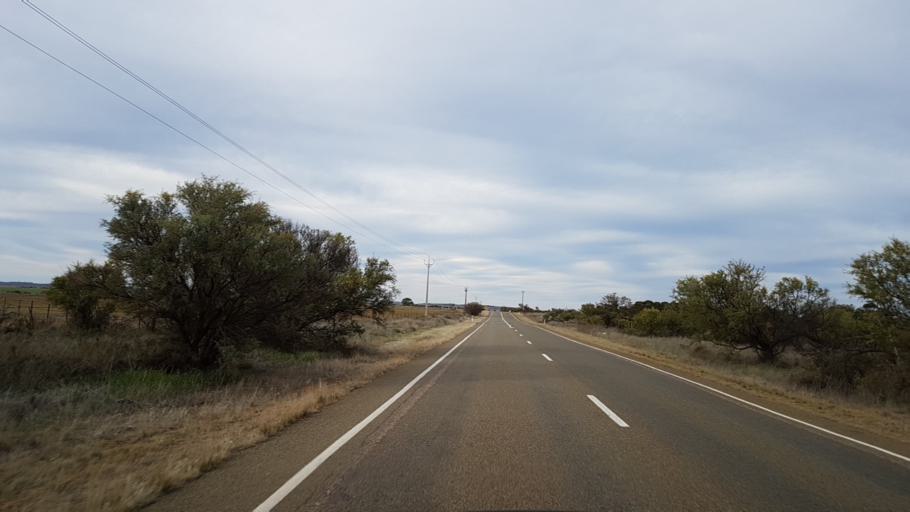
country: AU
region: South Australia
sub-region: Peterborough
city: Peterborough
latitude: -33.0032
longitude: 138.7745
